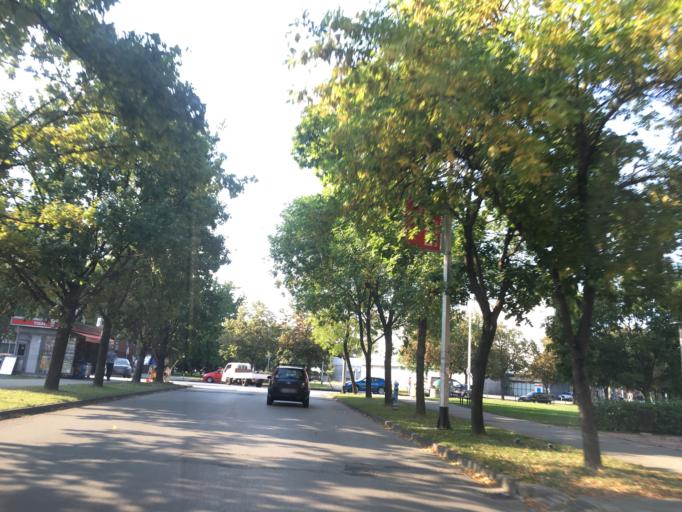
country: HR
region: Grad Zagreb
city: Jankomir
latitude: 45.7937
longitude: 15.9196
